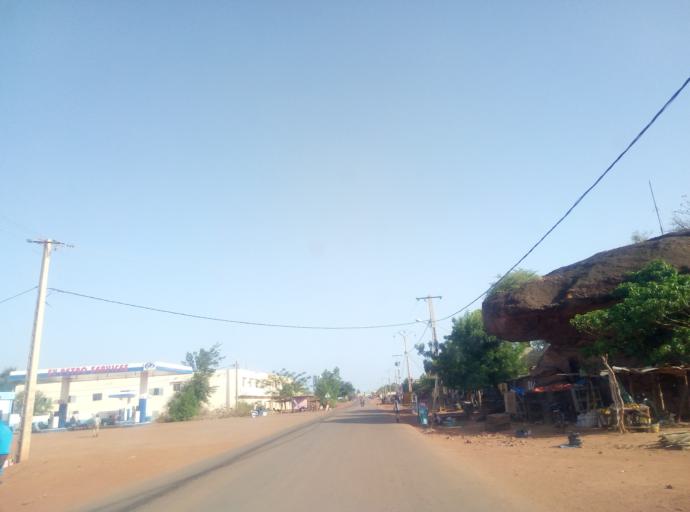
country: ML
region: Bamako
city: Bamako
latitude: 12.6082
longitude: -7.7727
